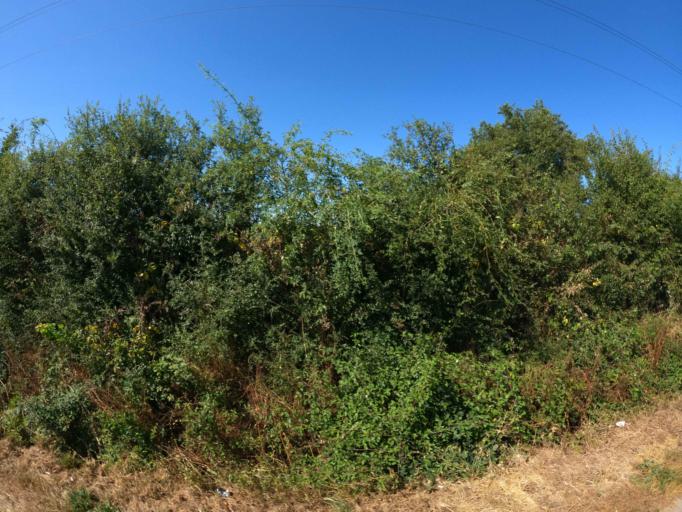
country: FR
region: Pays de la Loire
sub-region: Departement de la Vendee
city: Les Landes-Genusson
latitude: 46.9607
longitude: -1.1358
